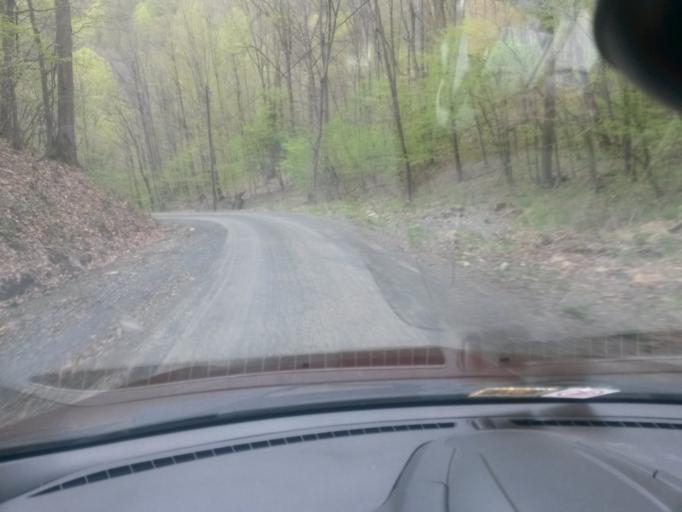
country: US
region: West Virginia
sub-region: Nicholas County
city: Richwood
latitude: 38.0532
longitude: -80.3515
